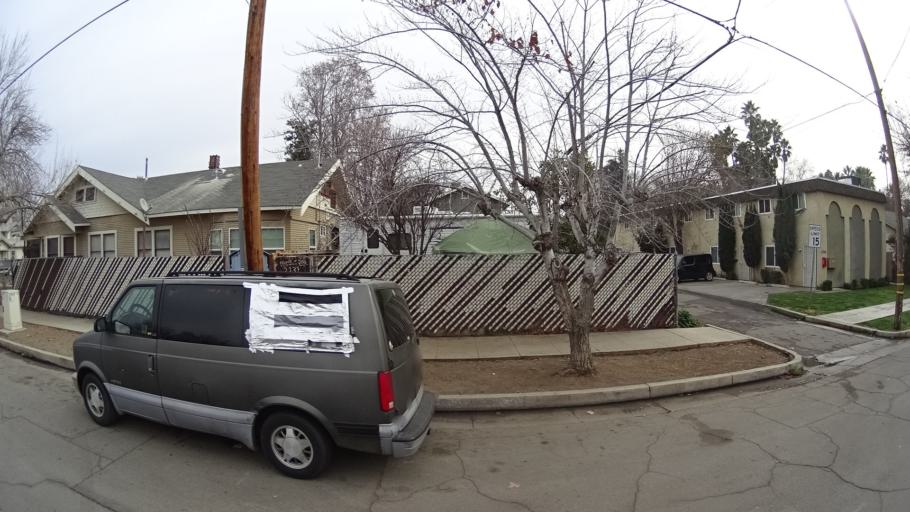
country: US
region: California
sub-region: Kern County
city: Bakersfield
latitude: 35.3671
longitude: -119.0275
